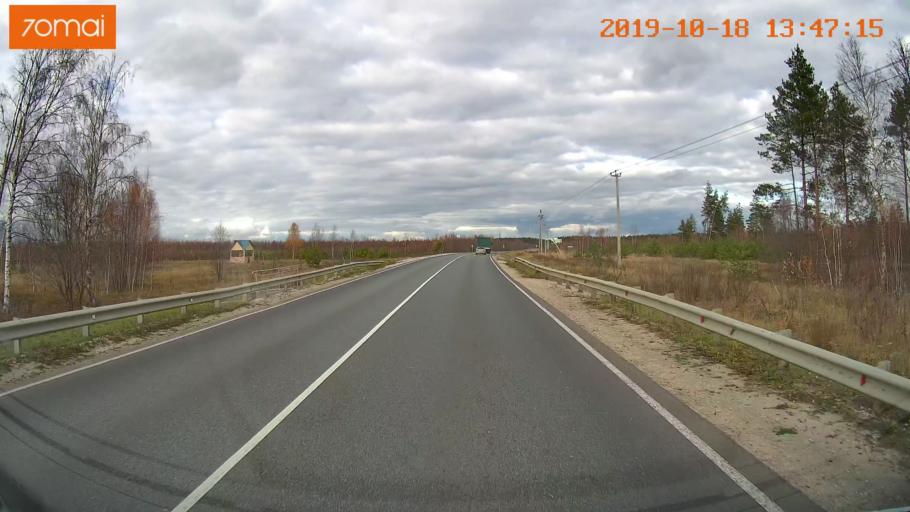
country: RU
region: Rjazan
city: Solotcha
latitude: 54.9718
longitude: 39.9513
